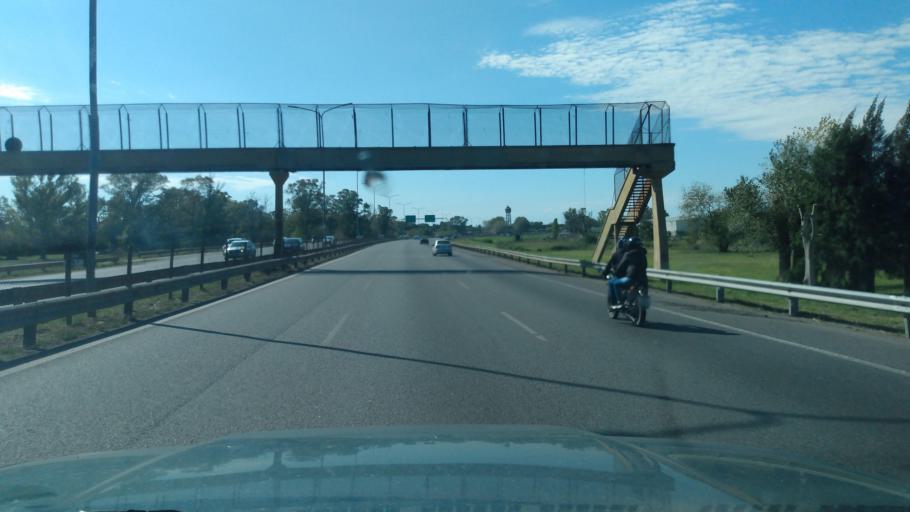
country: AR
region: Buenos Aires
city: Hurlingham
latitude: -34.5726
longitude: -58.6621
